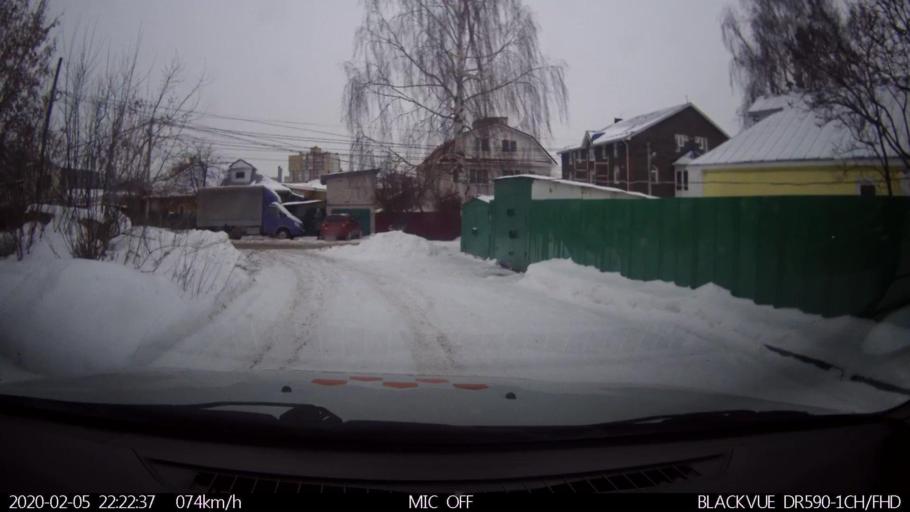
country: RU
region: Nizjnij Novgorod
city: Pervomaysk
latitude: 54.7649
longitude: 44.0152
